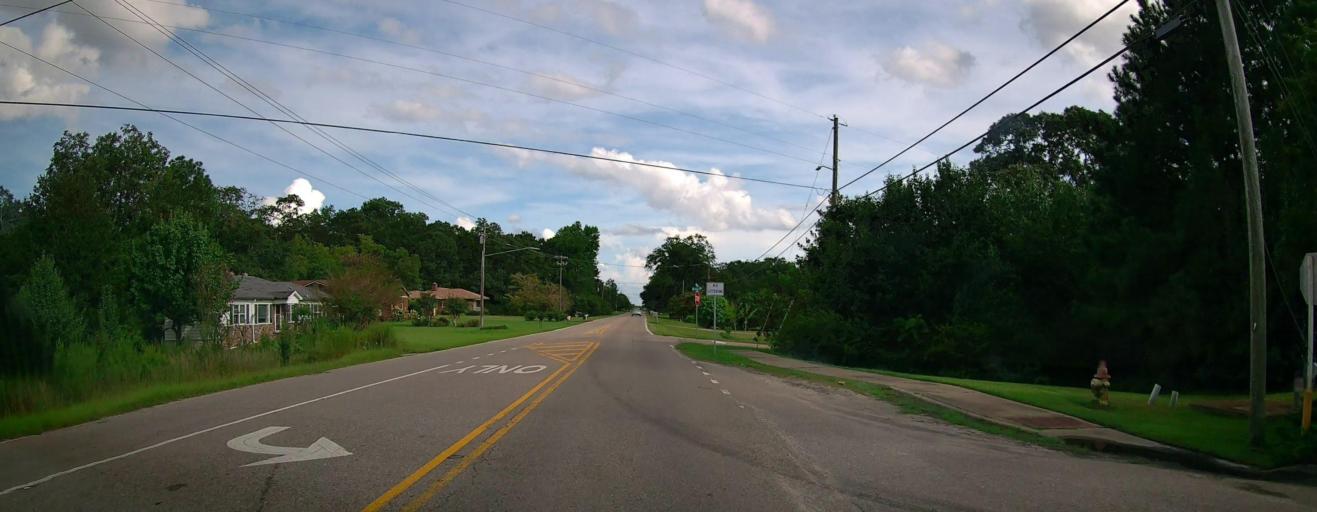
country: US
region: Alabama
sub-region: Russell County
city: Phenix City
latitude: 32.5196
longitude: -85.0282
